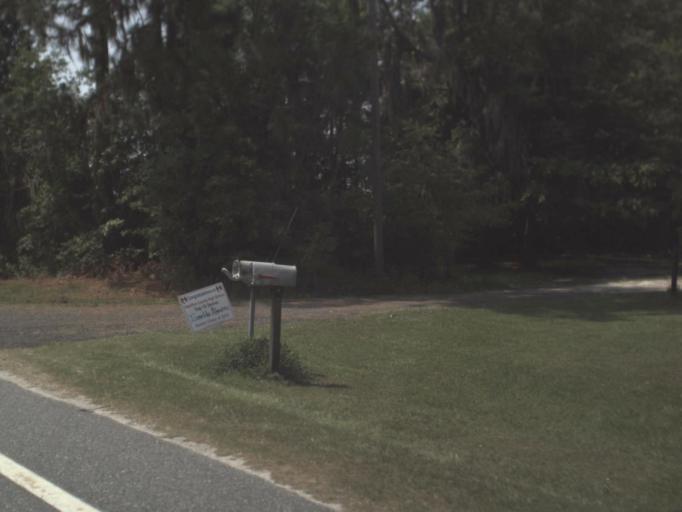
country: US
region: Georgia
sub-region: Echols County
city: Statenville
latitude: 30.6152
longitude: -83.1123
